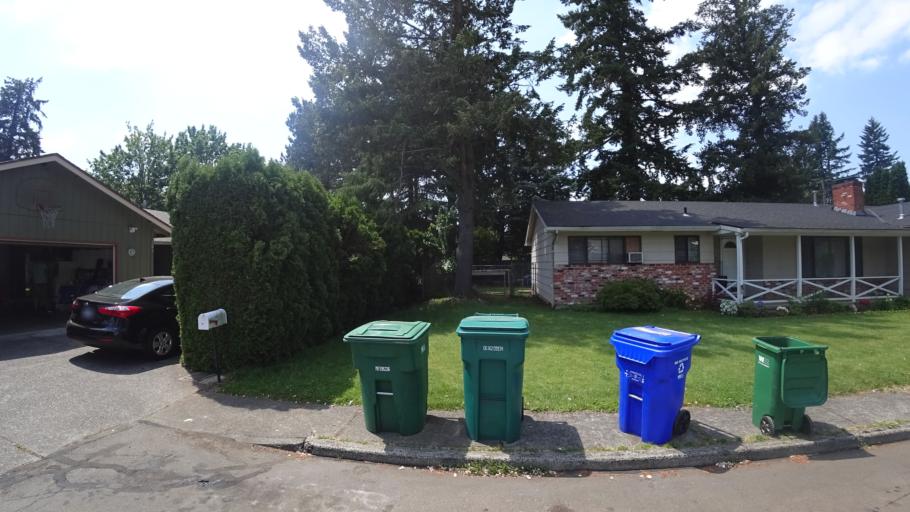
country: US
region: Oregon
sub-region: Multnomah County
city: Fairview
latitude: 45.5232
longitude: -122.4946
